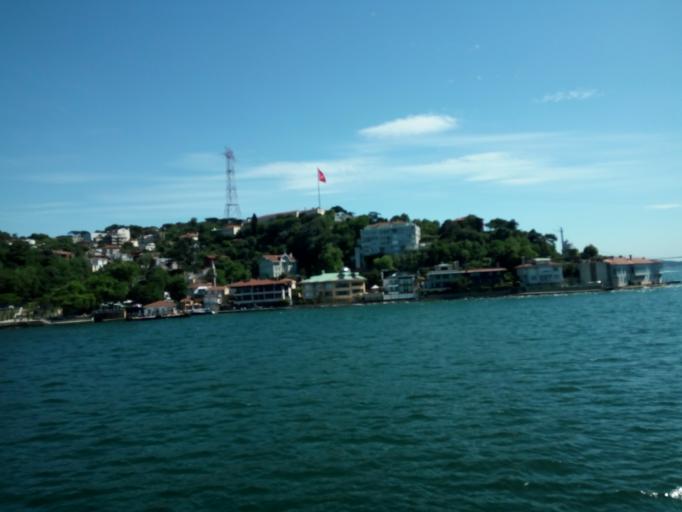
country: TR
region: Istanbul
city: UEskuedar
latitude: 41.0764
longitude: 29.0573
